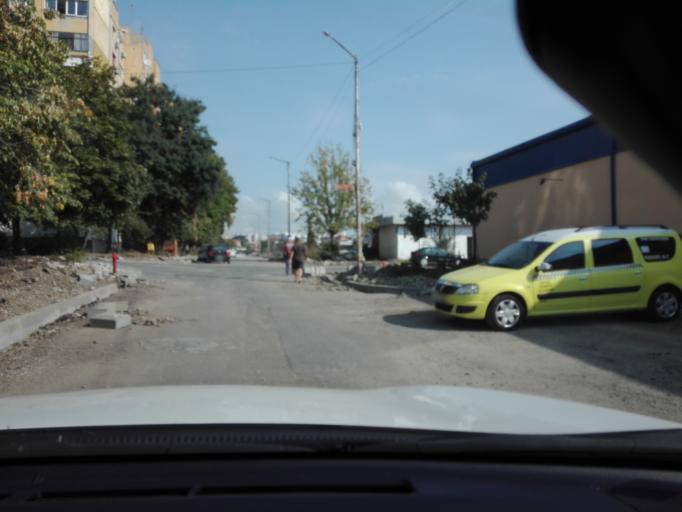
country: BG
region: Burgas
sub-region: Obshtina Burgas
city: Burgas
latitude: 42.4499
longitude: 27.4126
